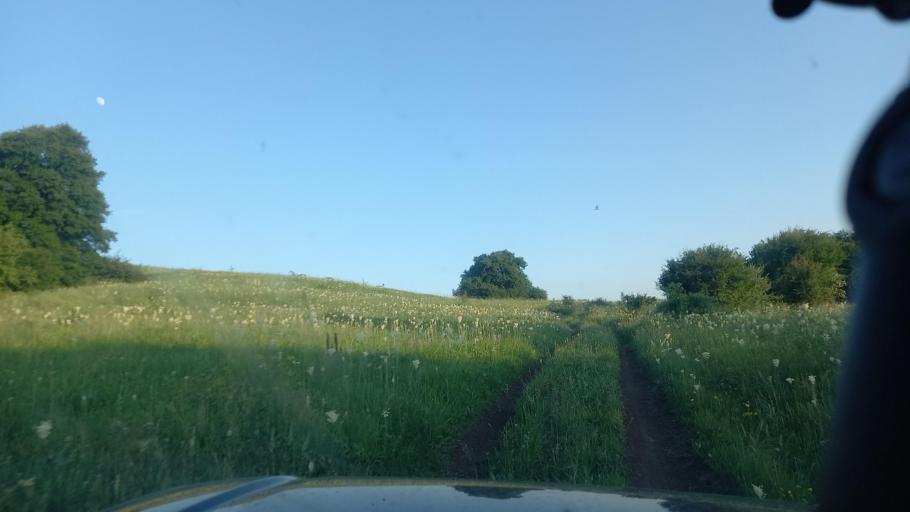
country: RU
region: Karachayevo-Cherkesiya
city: Kurdzhinovo
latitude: 44.1236
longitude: 41.0919
